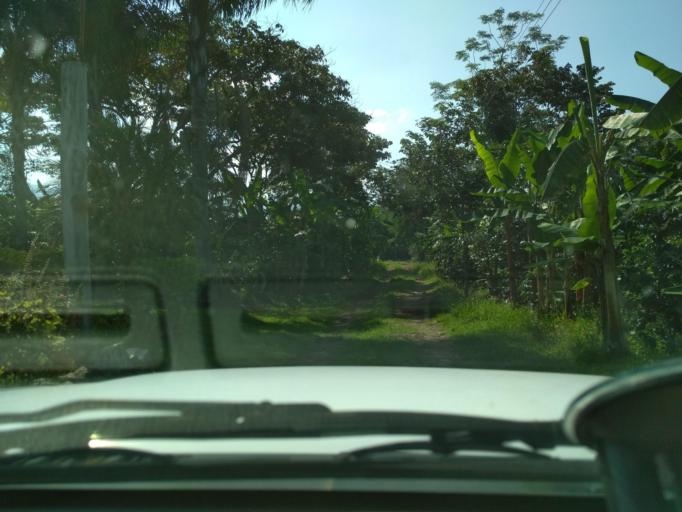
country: MX
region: Veracruz
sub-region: Chocaman
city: San Jose Neria
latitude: 18.9950
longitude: -96.9993
